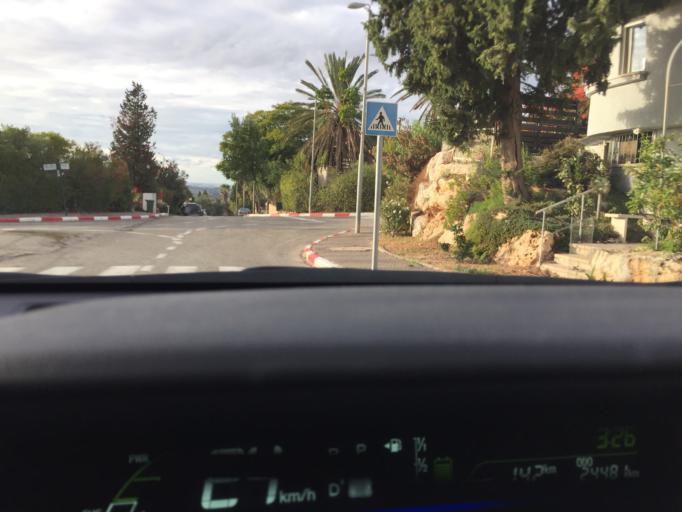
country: PS
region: West Bank
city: Az Zawiyah
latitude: 32.1084
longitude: 35.0338
